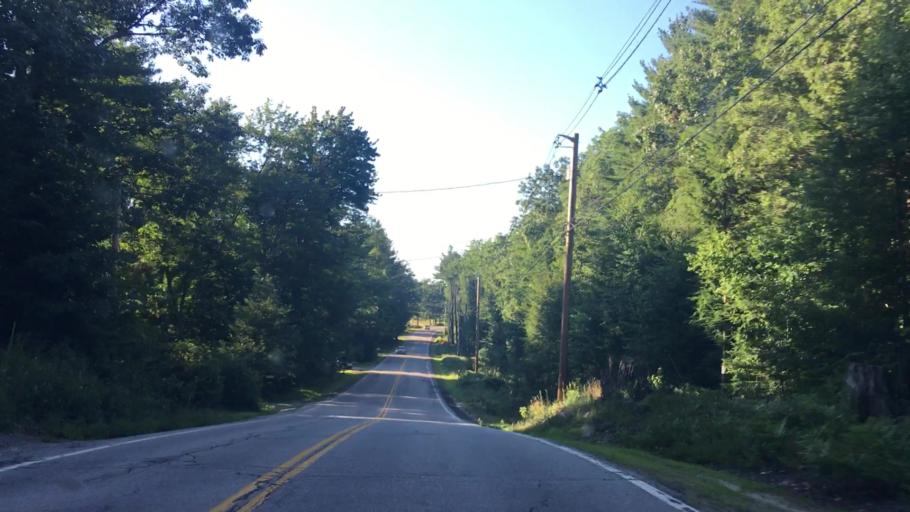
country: US
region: New Hampshire
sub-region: Rockingham County
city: Sandown
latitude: 42.9431
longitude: -71.1942
